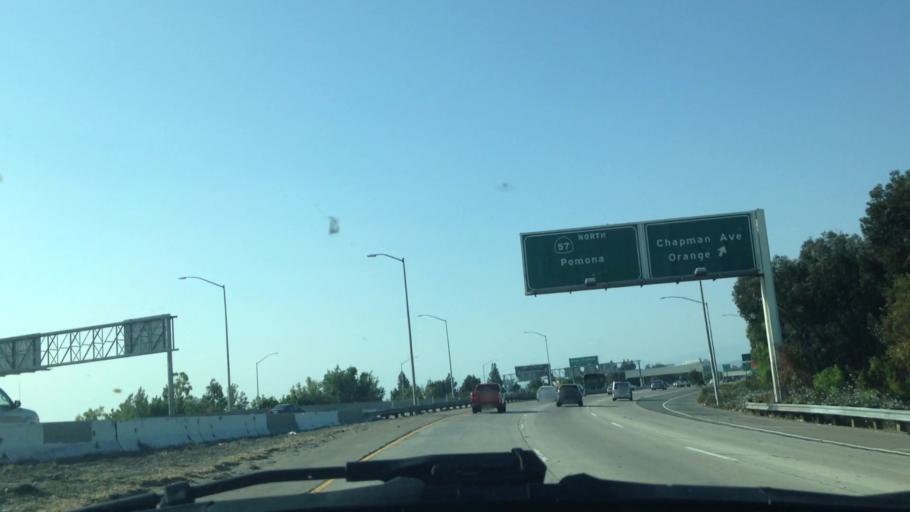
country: US
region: California
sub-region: Orange County
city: Orange
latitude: 33.7834
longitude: -117.8794
